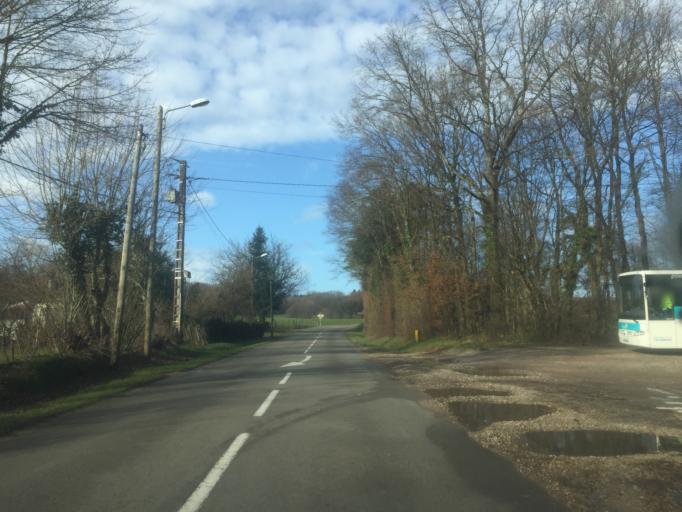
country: FR
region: Franche-Comte
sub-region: Departement du Doubs
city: Saint-Vit
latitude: 47.1872
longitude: 5.8108
